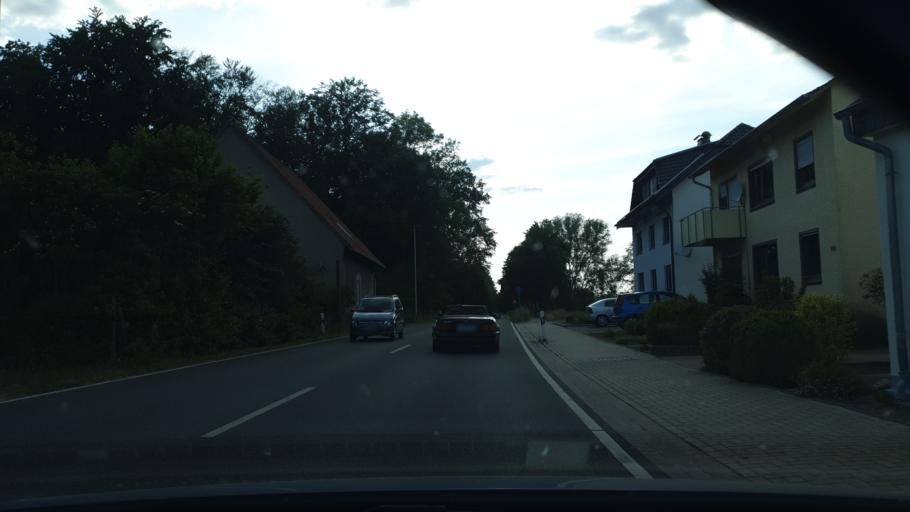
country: DE
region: North Rhine-Westphalia
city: Enger
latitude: 52.1763
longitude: 8.5399
